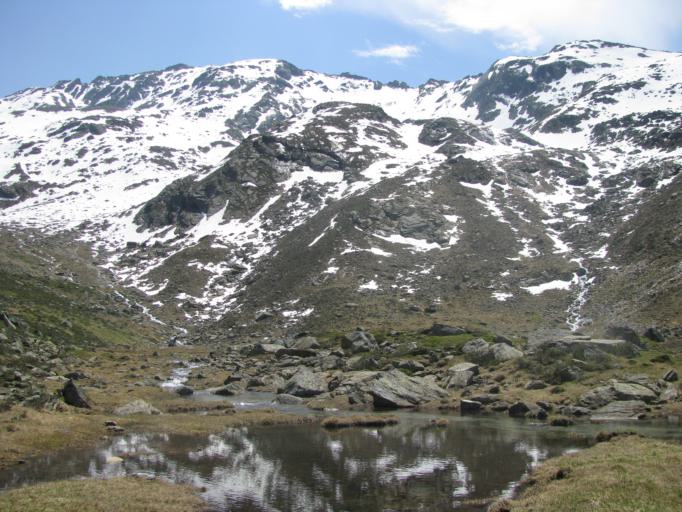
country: AT
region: Tyrol
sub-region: Politischer Bezirk Landeck
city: See
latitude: 47.0648
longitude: 10.5052
